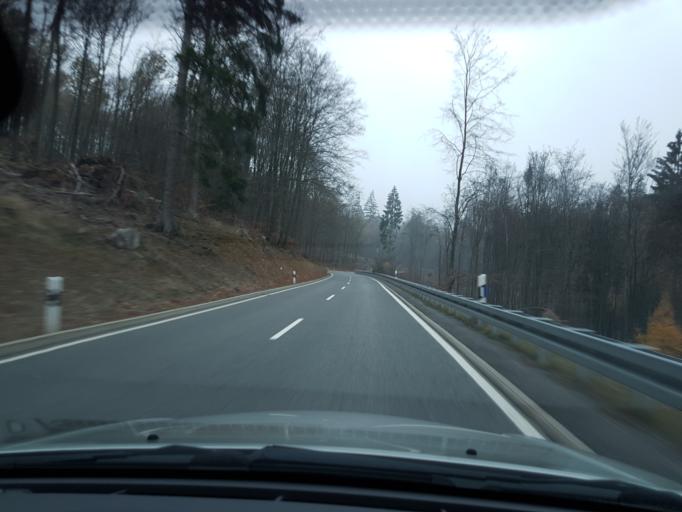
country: DE
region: Hesse
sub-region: Regierungsbezirk Darmstadt
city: Kiedrich
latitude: 50.0716
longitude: 8.0559
